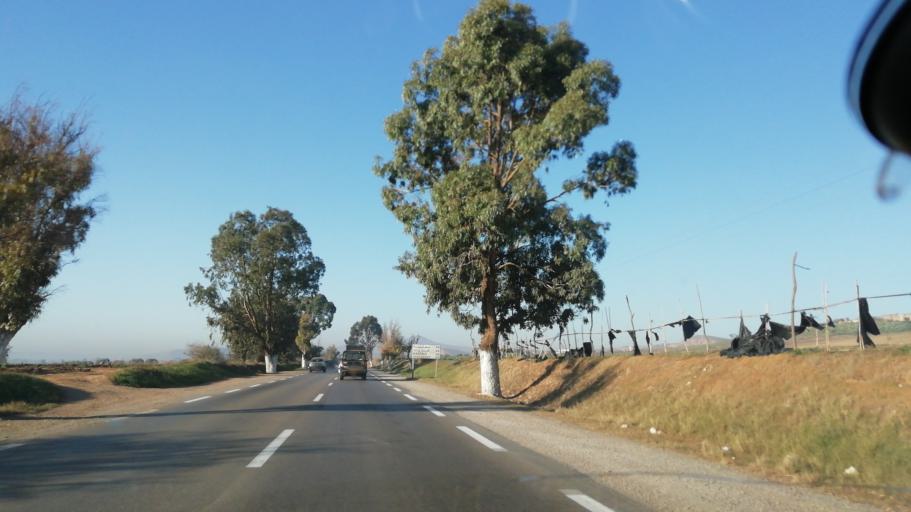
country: DZ
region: Tlemcen
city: Remchi
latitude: 35.0647
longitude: -1.4807
